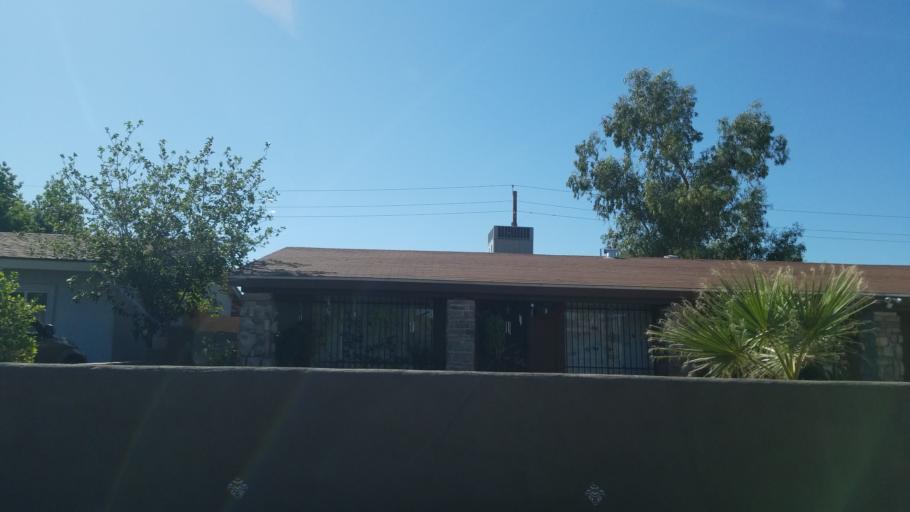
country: US
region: Arizona
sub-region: Maricopa County
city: Glendale
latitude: 33.4708
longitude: -112.1678
